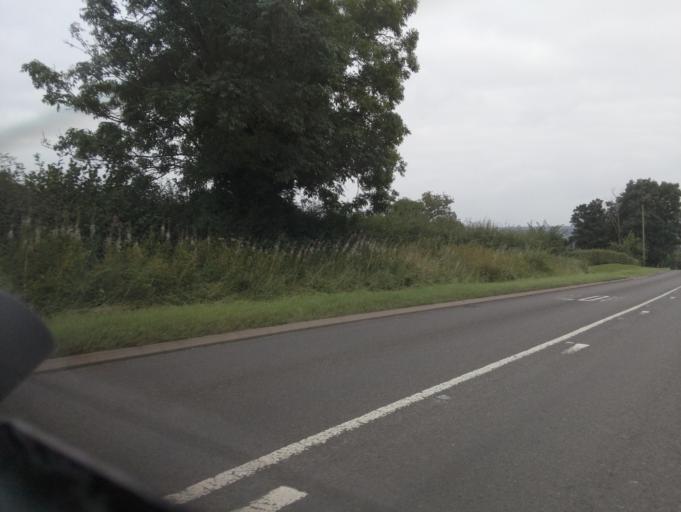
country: GB
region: England
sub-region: Staffordshire
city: Mayfield
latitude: 53.0155
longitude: -1.7789
